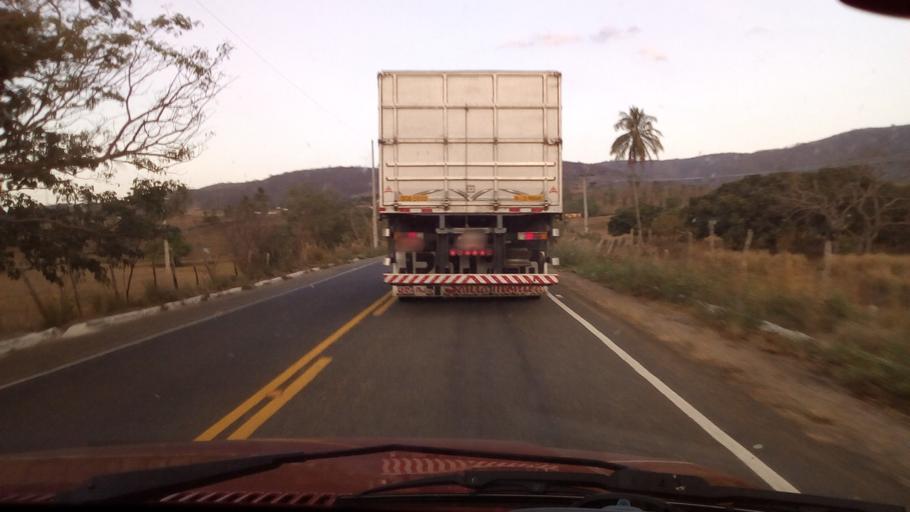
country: BR
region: Paraiba
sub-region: Bananeiras
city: Solanea
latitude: -6.7228
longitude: -35.5494
